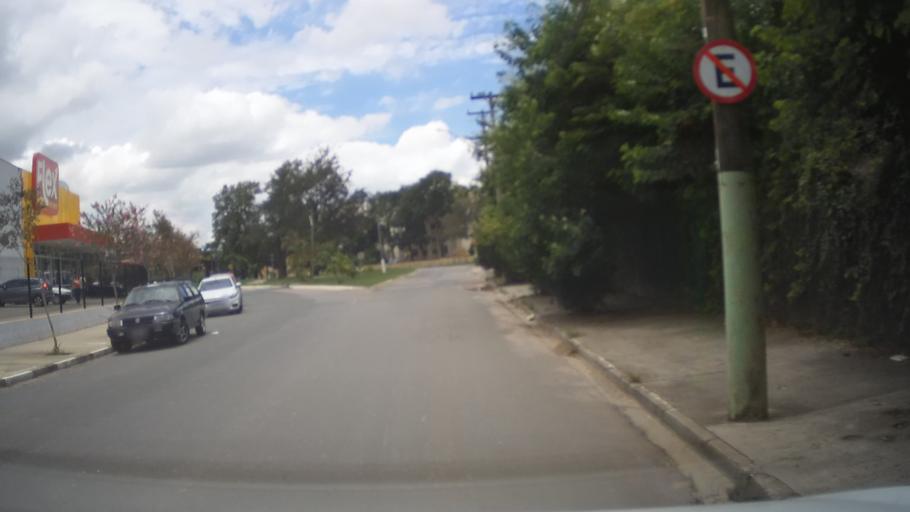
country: BR
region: Sao Paulo
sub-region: Valinhos
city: Valinhos
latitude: -22.9783
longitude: -46.9885
